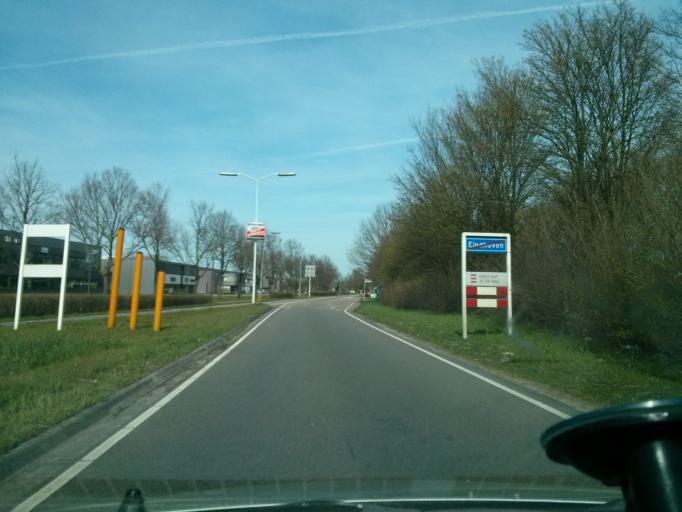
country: NL
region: North Brabant
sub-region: Gemeente Son en Breugel
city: Son
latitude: 51.4874
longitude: 5.4957
